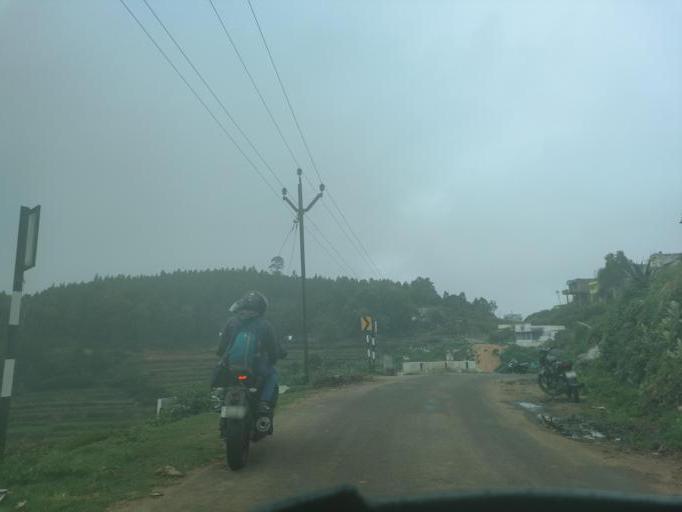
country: IN
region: Tamil Nadu
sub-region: Dindigul
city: Kodaikanal
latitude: 10.2229
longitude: 77.3472
